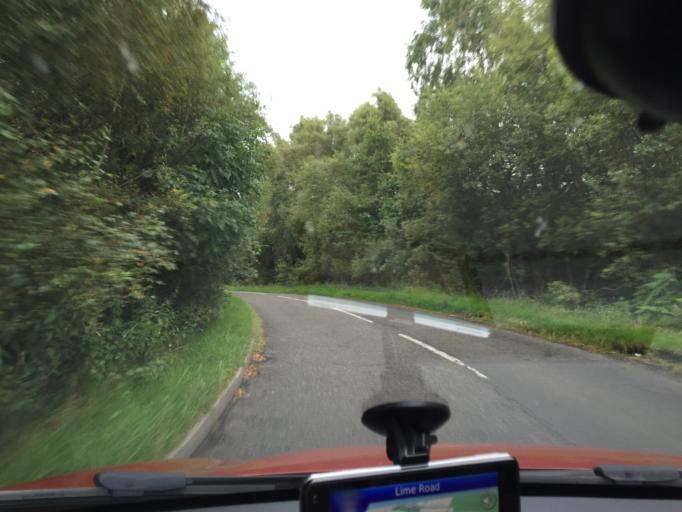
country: GB
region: Scotland
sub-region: Falkirk
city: Bonnybridge
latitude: 55.9926
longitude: -3.8523
